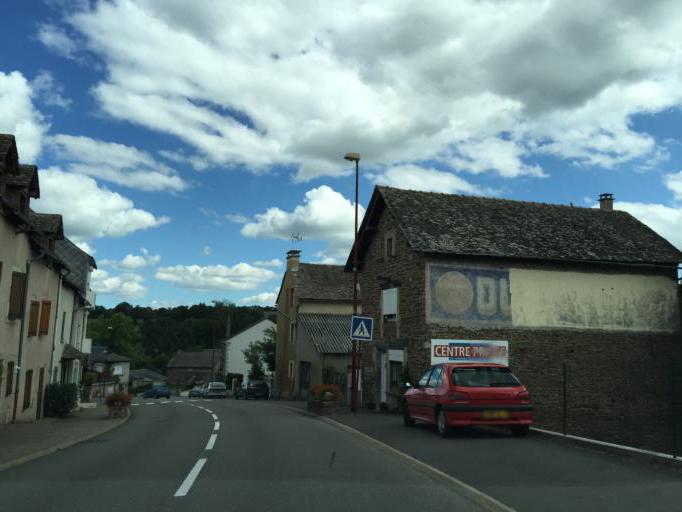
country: FR
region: Midi-Pyrenees
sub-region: Departement de l'Aveyron
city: Pont-de-Salars
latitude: 44.2831
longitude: 2.7257
